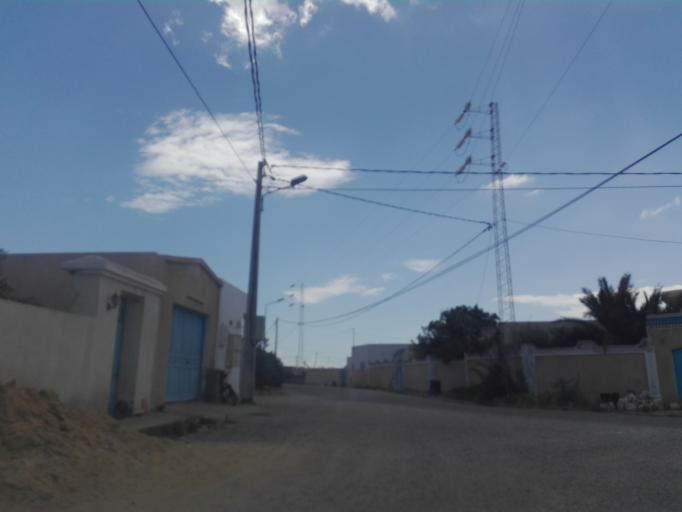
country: TN
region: Safaqis
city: Jabinyanah
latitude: 34.8198
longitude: 11.2528
